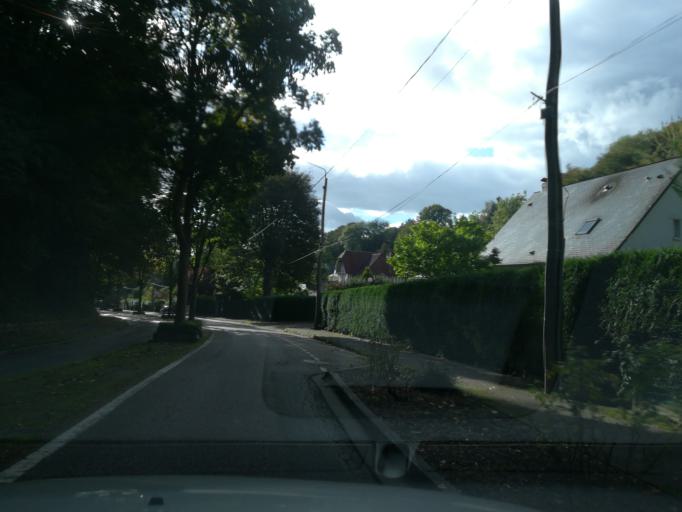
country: FR
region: Haute-Normandie
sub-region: Departement de la Seine-Maritime
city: Mont-Saint-Aignan
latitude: 49.4685
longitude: 1.1062
